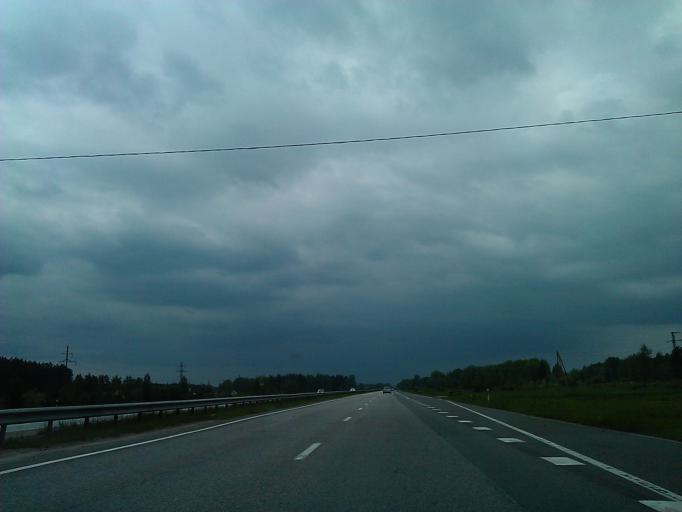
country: LV
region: Olaine
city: Olaine
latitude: 56.8161
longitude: 24.0112
